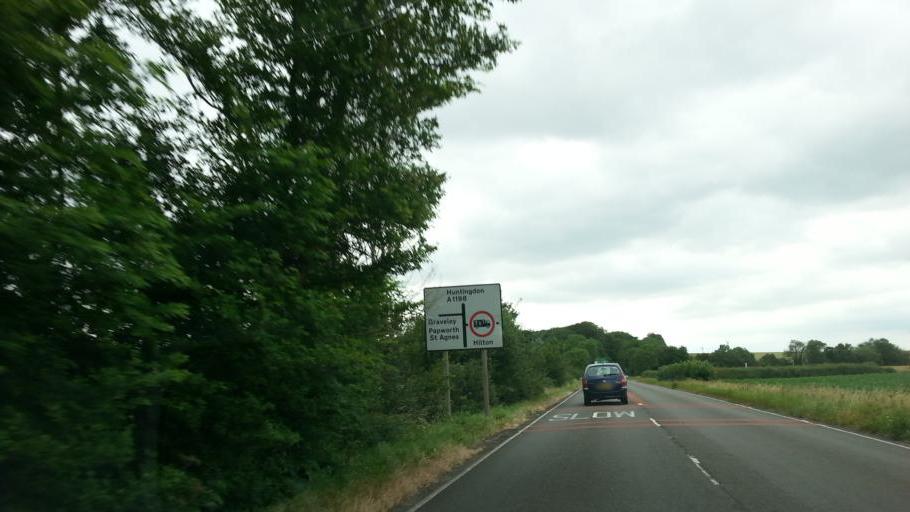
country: GB
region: England
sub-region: Cambridgeshire
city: Papworth Everard
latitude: 52.2740
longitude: -0.1362
